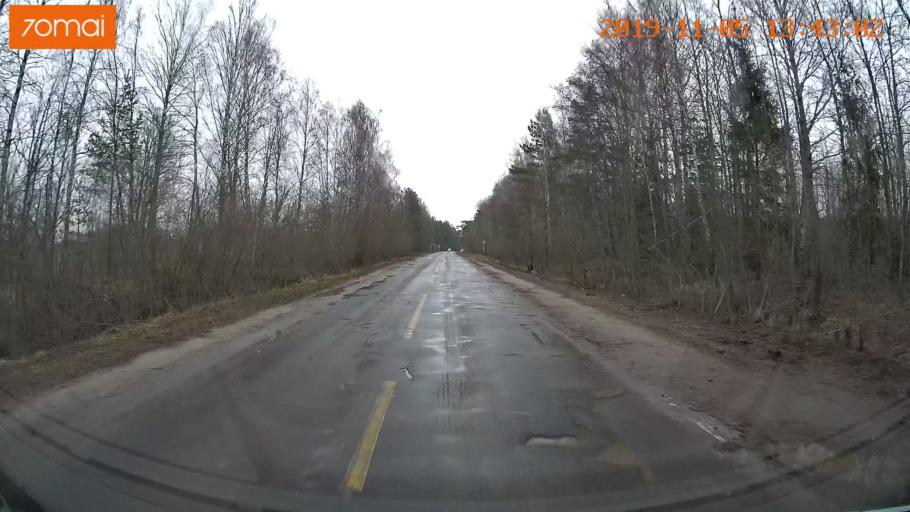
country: RU
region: Ivanovo
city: Shuya
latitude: 56.9707
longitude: 41.3996
